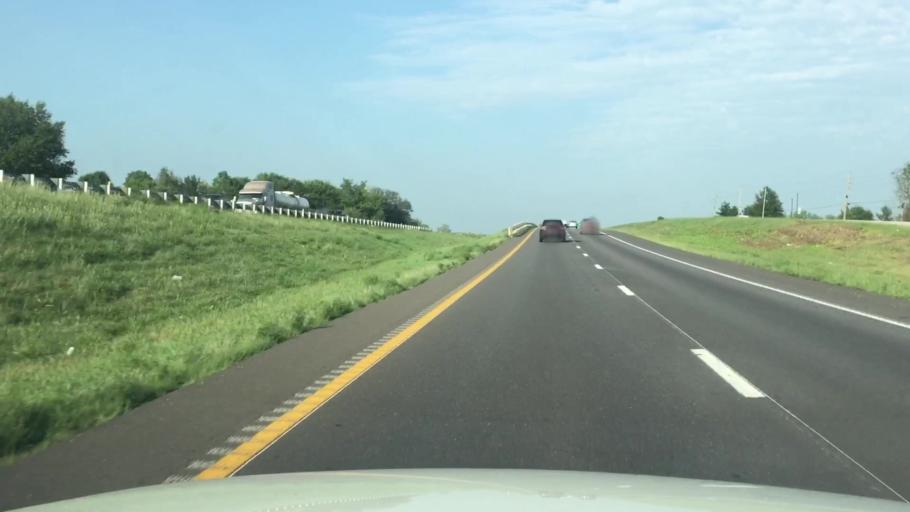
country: US
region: Missouri
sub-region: Clay County
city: Liberty
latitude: 39.2750
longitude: -94.4278
